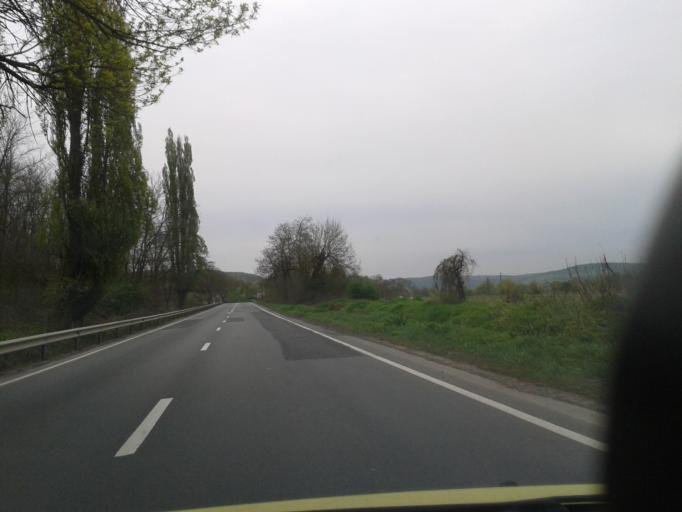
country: RO
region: Arad
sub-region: Comuna Conop
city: Conop
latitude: 46.1094
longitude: 21.8620
